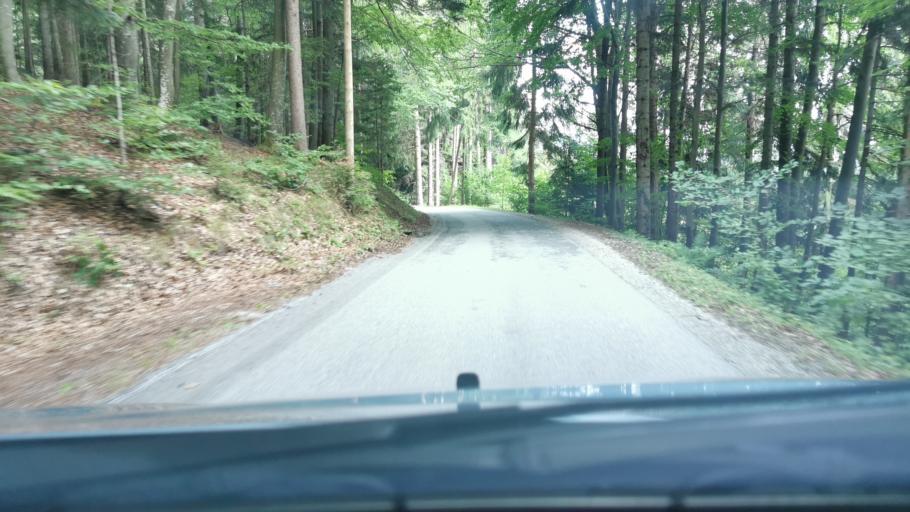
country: AT
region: Styria
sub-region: Politischer Bezirk Weiz
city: Koglhof
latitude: 47.3220
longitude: 15.6667
